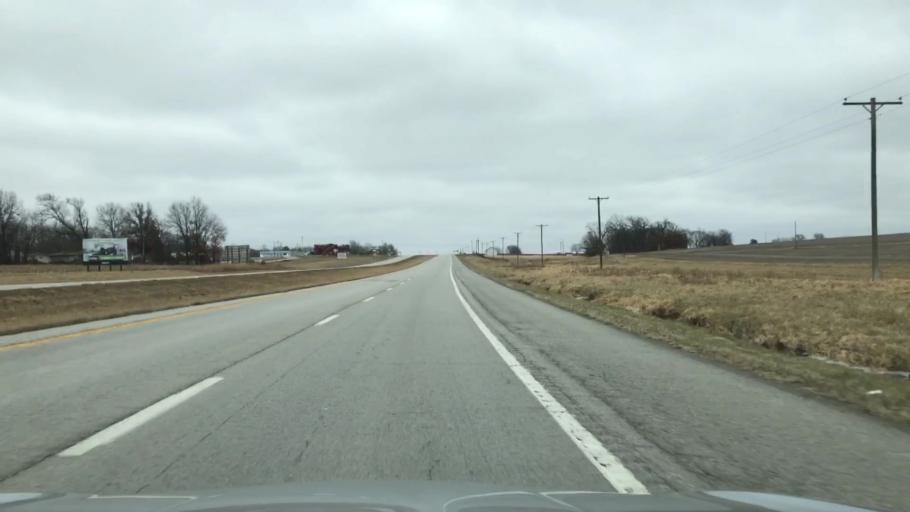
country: US
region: Missouri
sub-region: Livingston County
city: Chillicothe
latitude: 39.7753
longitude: -93.5278
